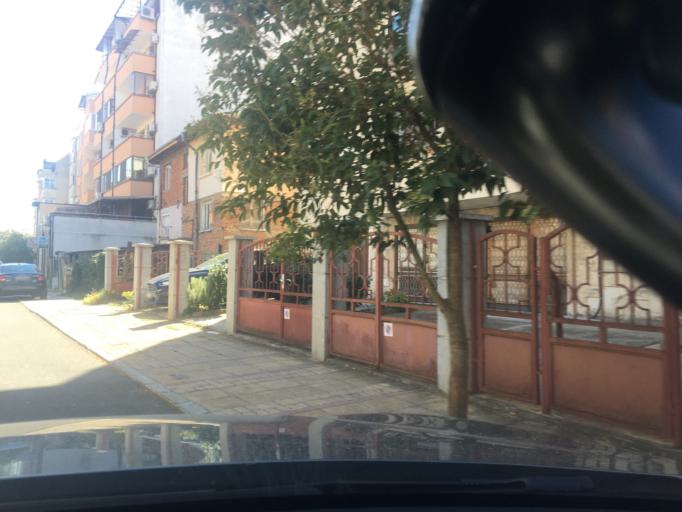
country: BG
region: Burgas
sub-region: Obshtina Burgas
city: Burgas
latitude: 42.5082
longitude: 27.4736
